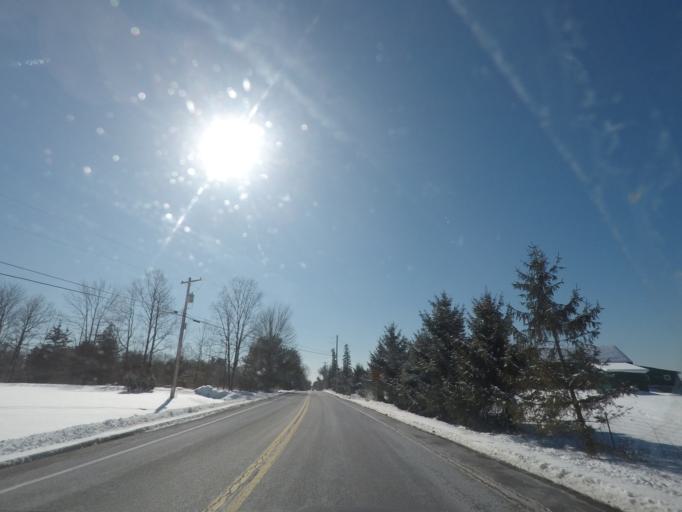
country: US
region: New York
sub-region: Saratoga County
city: Ballston Spa
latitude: 42.9858
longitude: -73.8330
